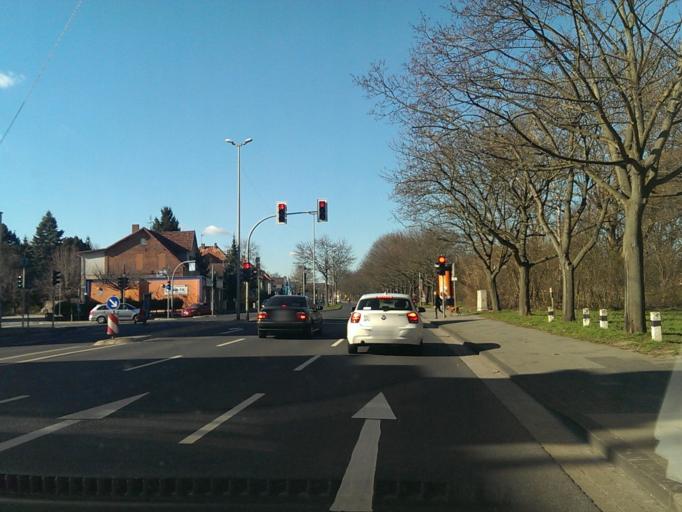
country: DE
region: Lower Saxony
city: Hildesheim
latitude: 52.1449
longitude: 9.9394
